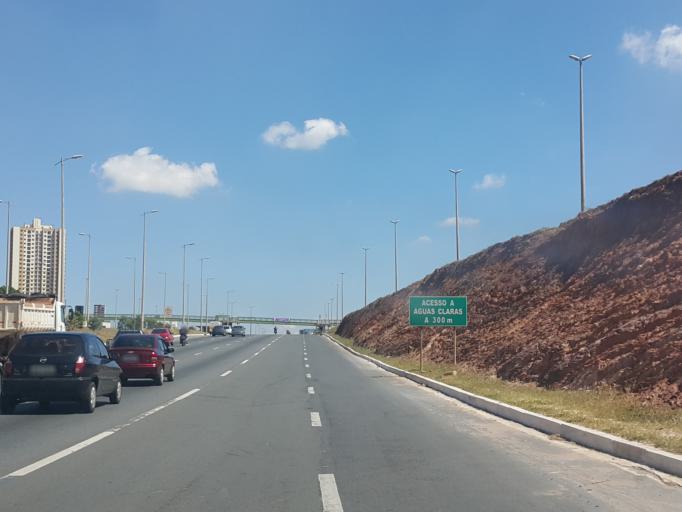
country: BR
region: Federal District
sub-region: Brasilia
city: Brasilia
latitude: -15.8302
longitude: -48.0399
